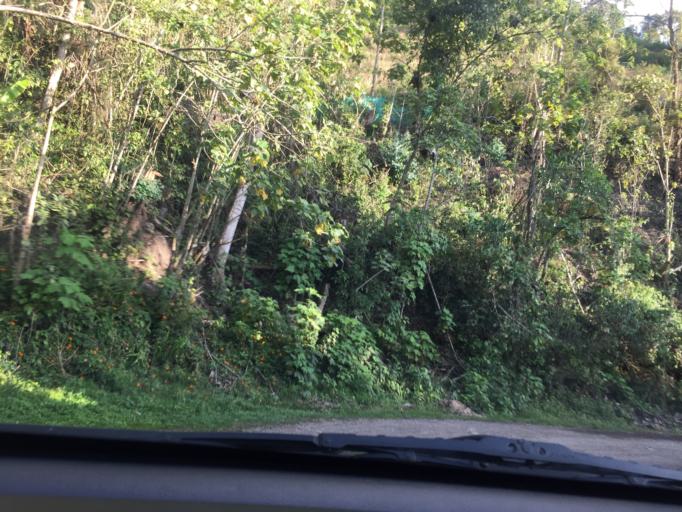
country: CO
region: Cundinamarca
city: Zipacon
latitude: 4.7198
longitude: -74.3897
